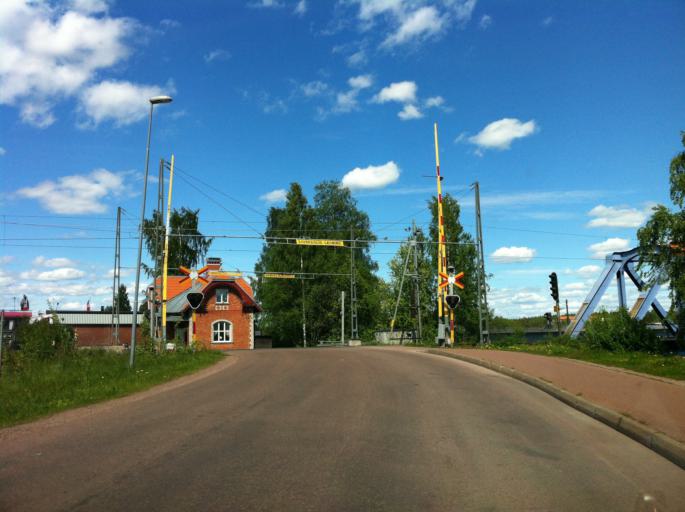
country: SE
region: Dalarna
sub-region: Mora Kommun
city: Mora
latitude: 61.0071
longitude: 14.5641
